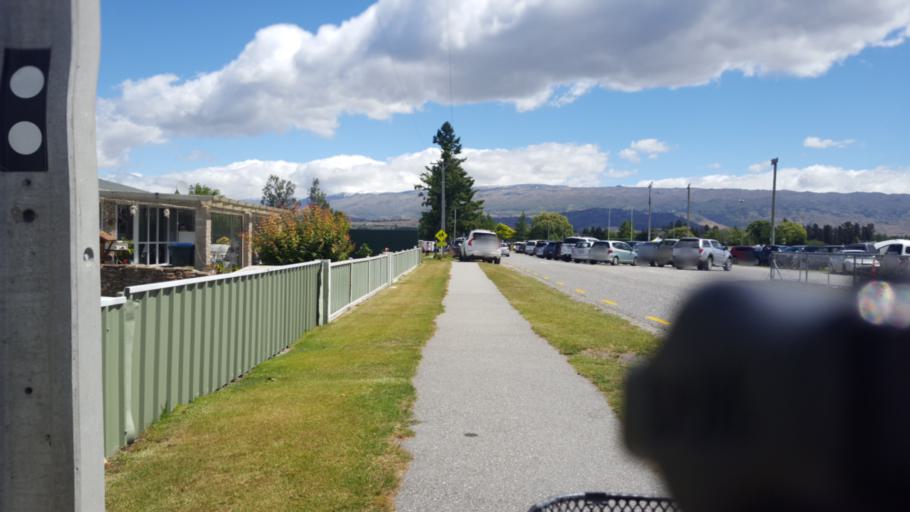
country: NZ
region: Otago
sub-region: Queenstown-Lakes District
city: Wanaka
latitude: -45.2417
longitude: 169.3886
